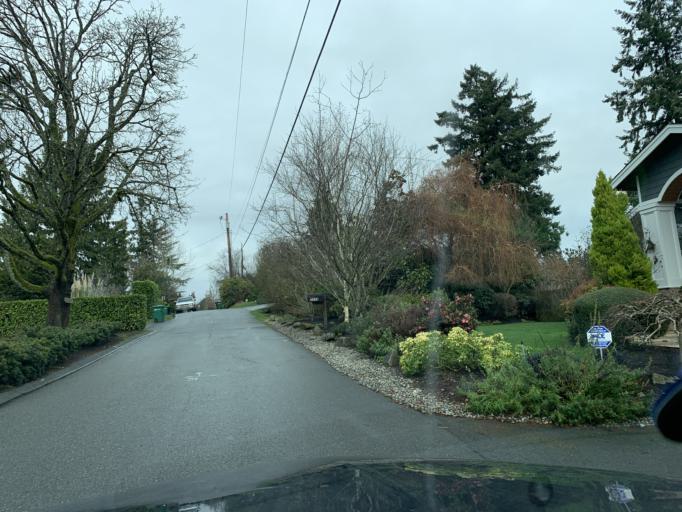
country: US
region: Washington
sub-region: King County
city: Mercer Island
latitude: 47.5899
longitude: -122.2295
